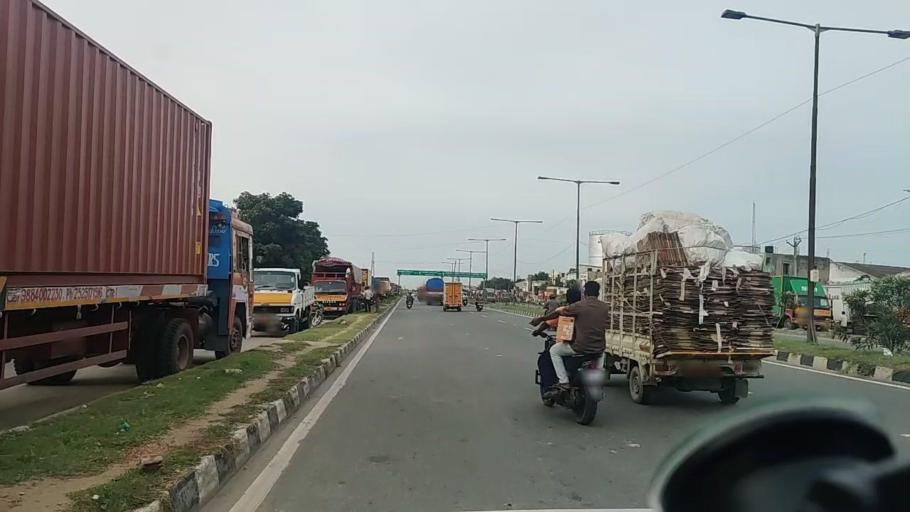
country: IN
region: Tamil Nadu
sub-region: Thiruvallur
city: Chinnasekkadu
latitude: 13.1495
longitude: 80.2221
